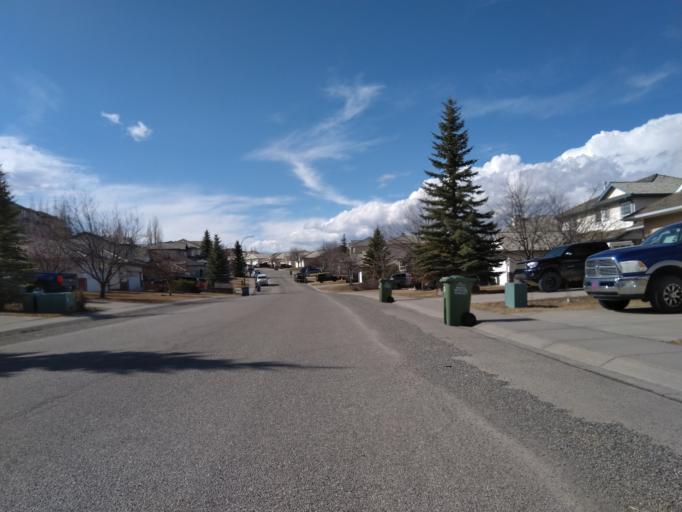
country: CA
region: Alberta
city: Cochrane
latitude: 51.1857
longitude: -114.5090
